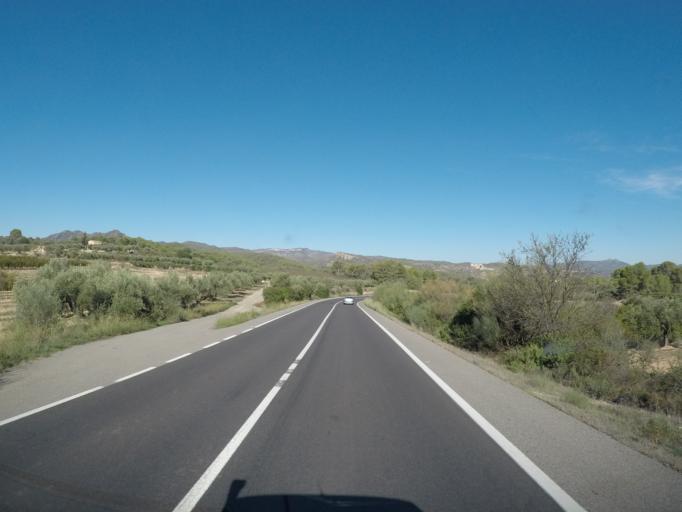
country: ES
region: Catalonia
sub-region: Provincia de Tarragona
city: Rasquera
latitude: 41.0169
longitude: 0.6101
